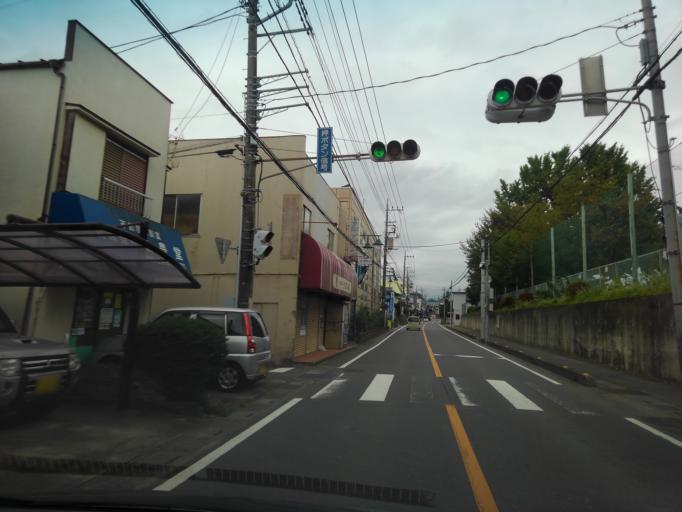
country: JP
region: Saitama
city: Tokorozawa
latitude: 35.7906
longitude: 139.4360
